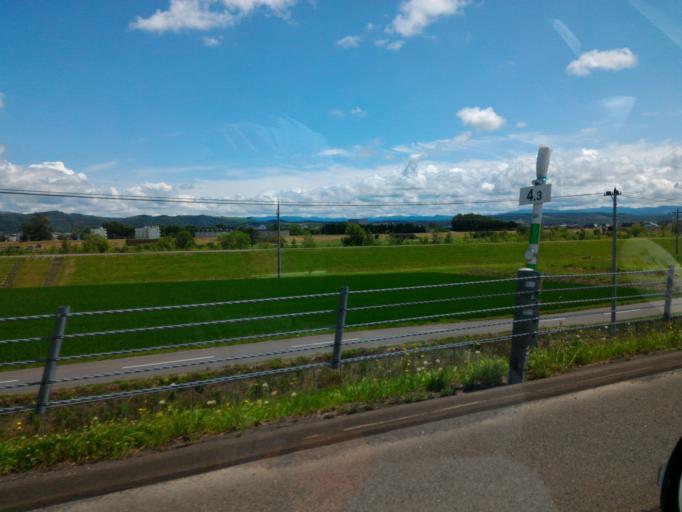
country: JP
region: Hokkaido
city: Nayoro
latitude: 44.3559
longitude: 142.4358
